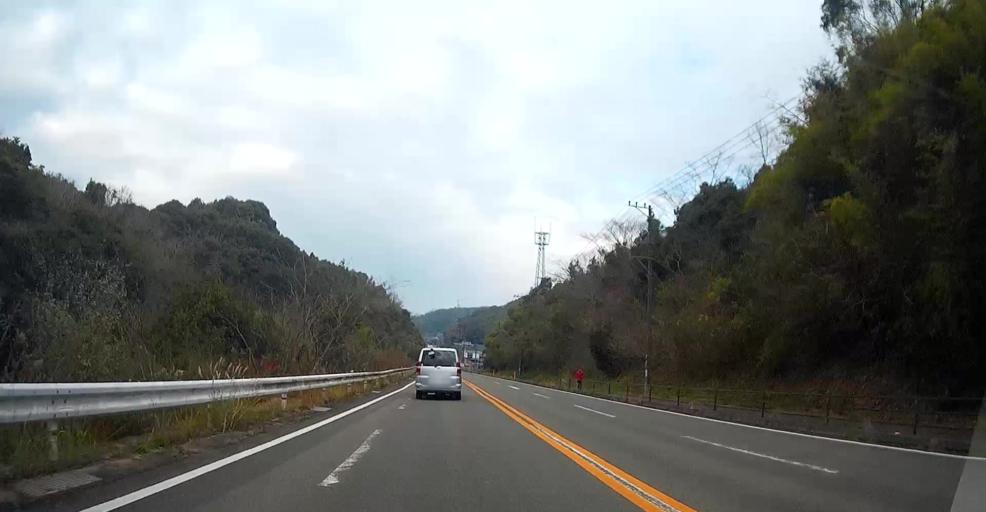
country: JP
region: Kumamoto
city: Yatsushiro
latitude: 32.5596
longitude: 130.4146
